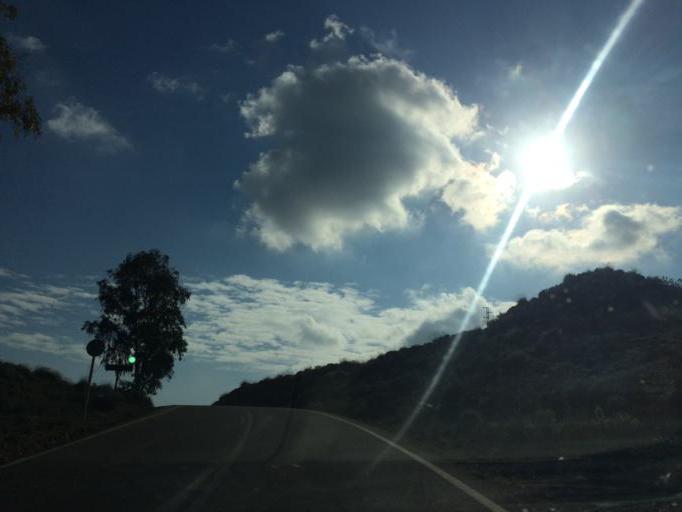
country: ES
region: Andalusia
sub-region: Provincia de Almeria
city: San Jose
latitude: 36.8302
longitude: -2.0406
